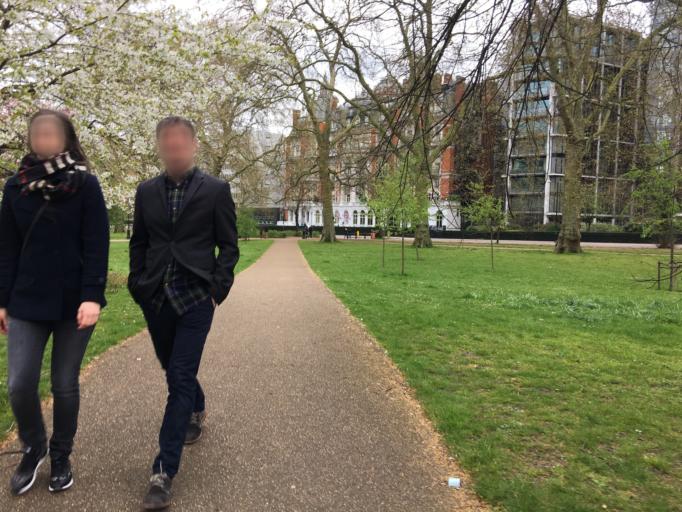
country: GB
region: England
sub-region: Greater London
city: Chelsea
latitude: 51.5031
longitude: -0.1618
